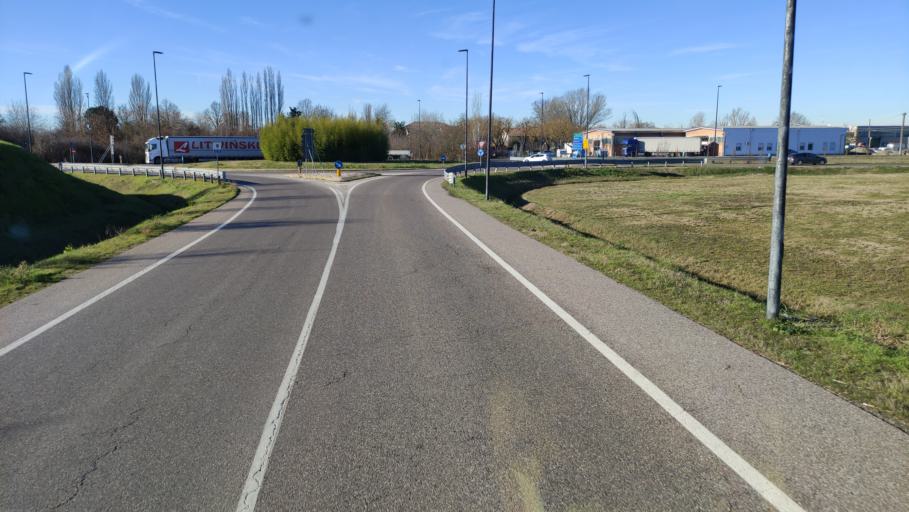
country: IT
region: Emilia-Romagna
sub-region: Provincia di Reggio Emilia
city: Novellara
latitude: 44.8531
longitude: 10.7381
